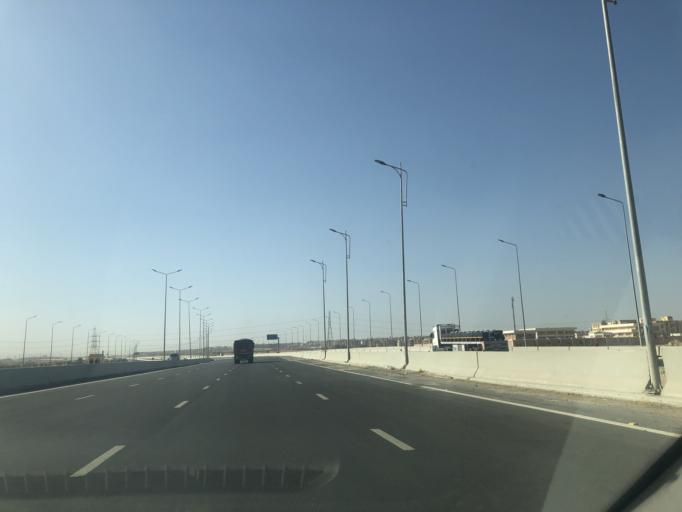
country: EG
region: Al Jizah
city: Madinat Sittah Uktubar
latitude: 29.9621
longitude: 30.8903
